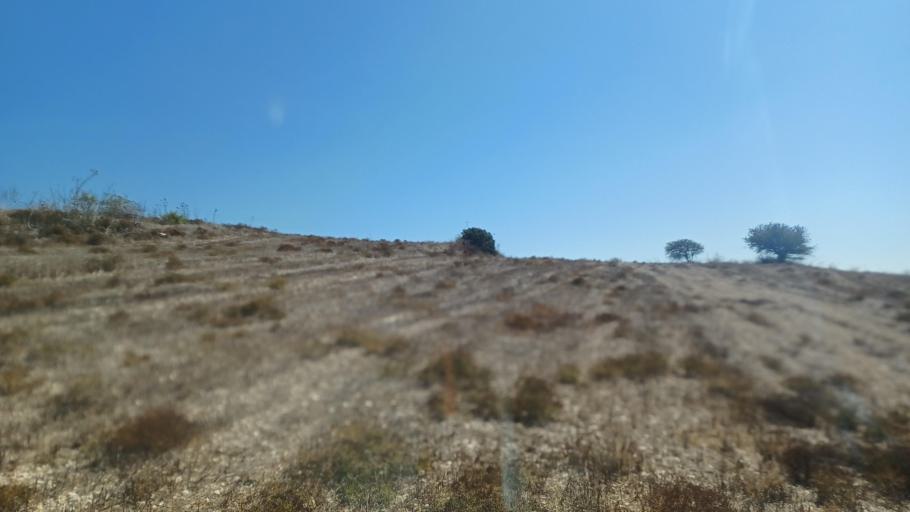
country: CY
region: Pafos
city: Mesogi
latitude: 34.8150
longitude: 32.4886
